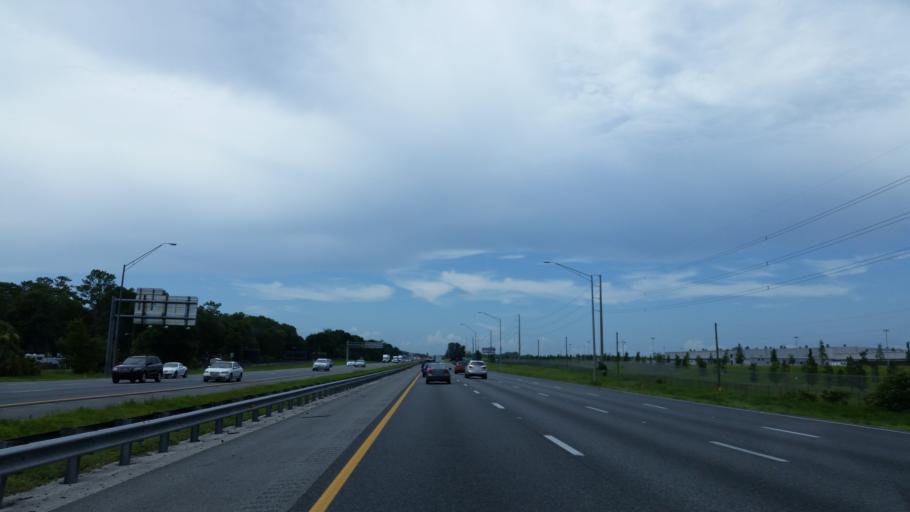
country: US
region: Florida
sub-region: Marion County
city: Ocala
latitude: 29.2114
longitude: -82.1844
